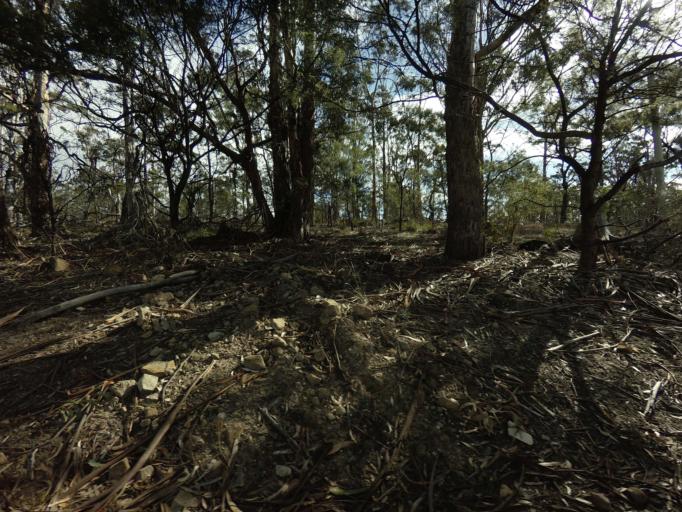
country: AU
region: Tasmania
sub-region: Sorell
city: Sorell
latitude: -42.3306
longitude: 147.9675
